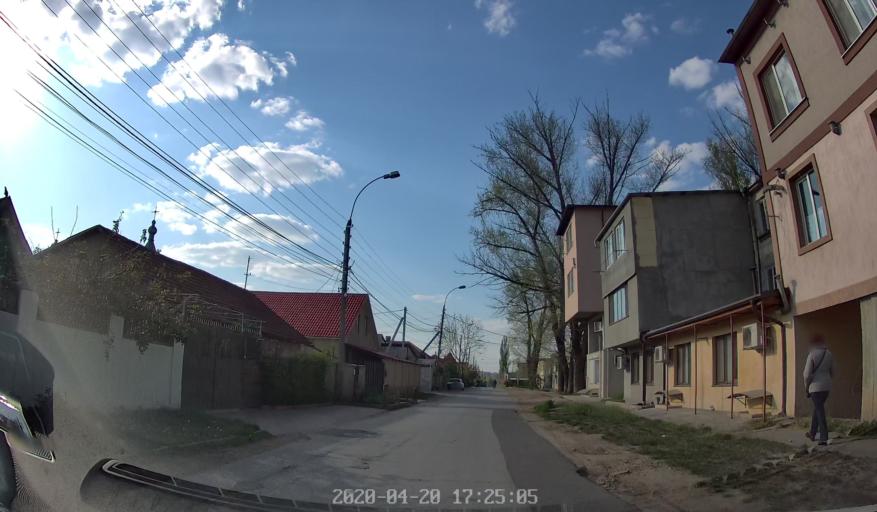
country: MD
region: Chisinau
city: Chisinau
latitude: 46.9919
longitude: 28.8771
